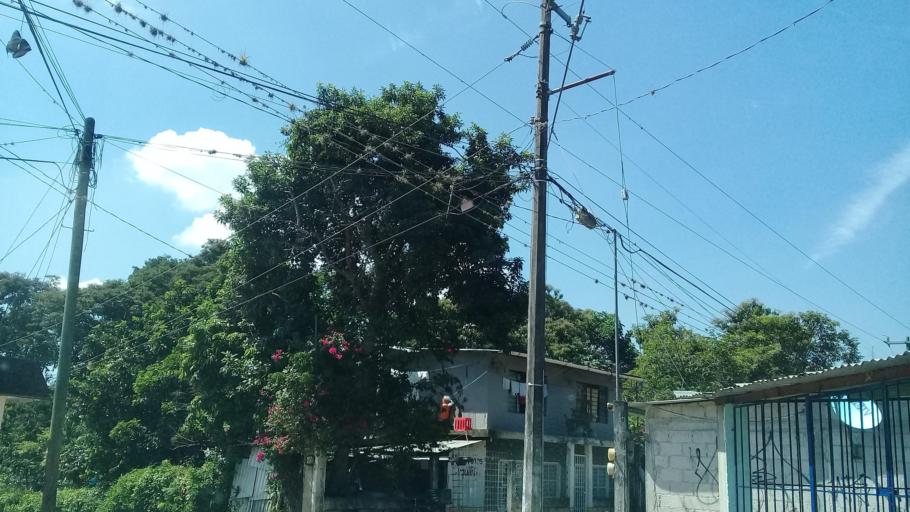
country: MX
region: Veracruz
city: Amatlan de los Reyes
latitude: 18.8415
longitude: -96.9169
